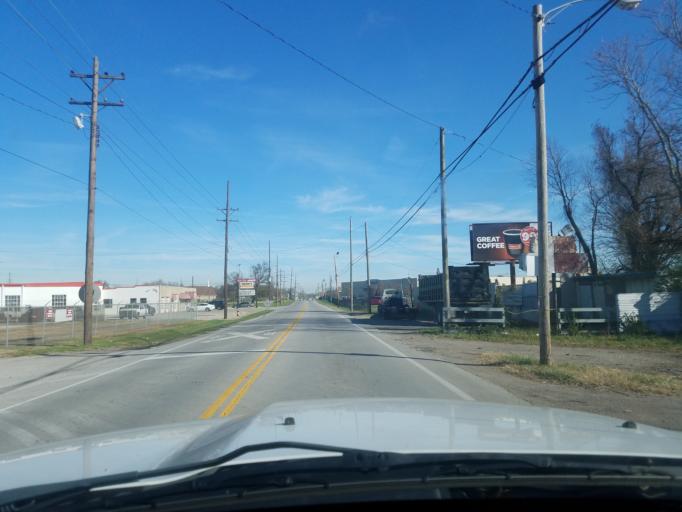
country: US
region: Kentucky
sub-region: Jefferson County
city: Shively
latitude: 38.2166
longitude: -85.8167
